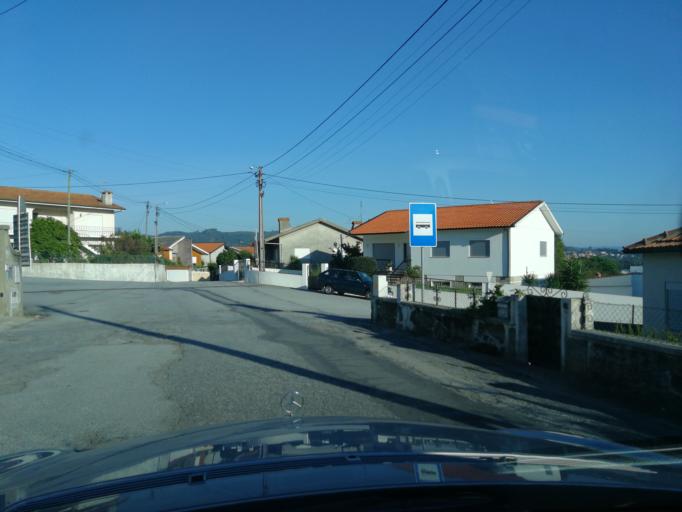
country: PT
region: Braga
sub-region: Vila Nova de Famalicao
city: Vila Nova de Famalicao
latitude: 41.4299
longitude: -8.5073
